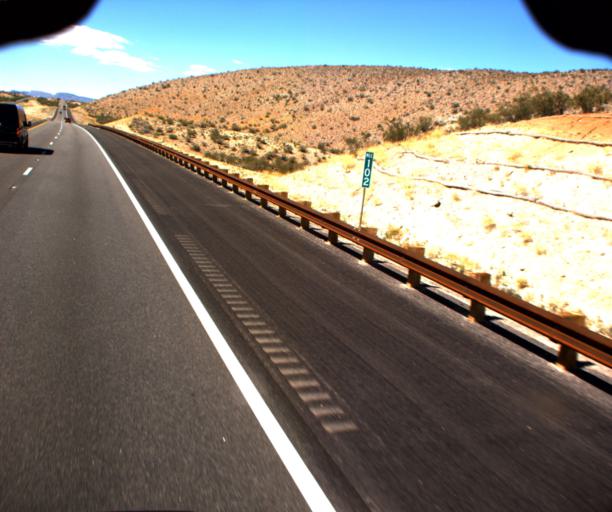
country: US
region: Arizona
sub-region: Mohave County
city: Kingman
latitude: 35.0127
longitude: -113.6639
